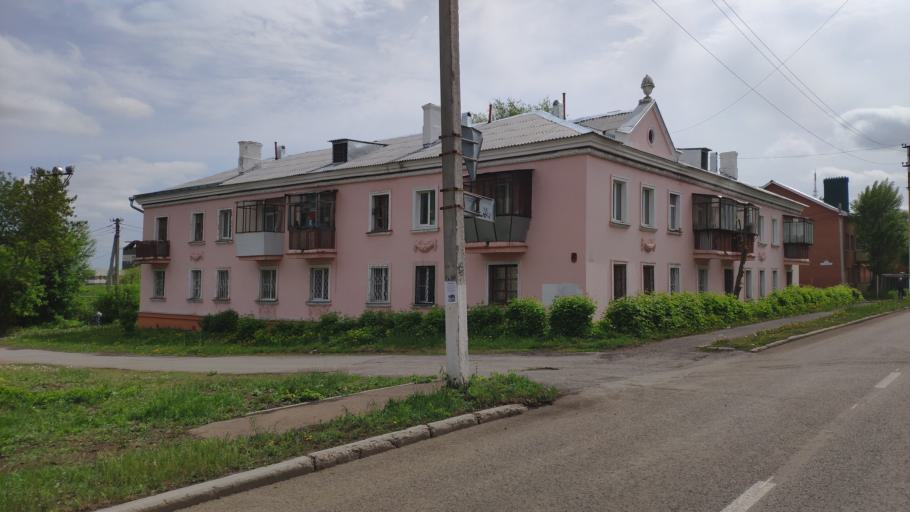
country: RU
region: Chelyabinsk
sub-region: Gorod Magnitogorsk
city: Magnitogorsk
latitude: 53.4212
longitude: 58.9569
